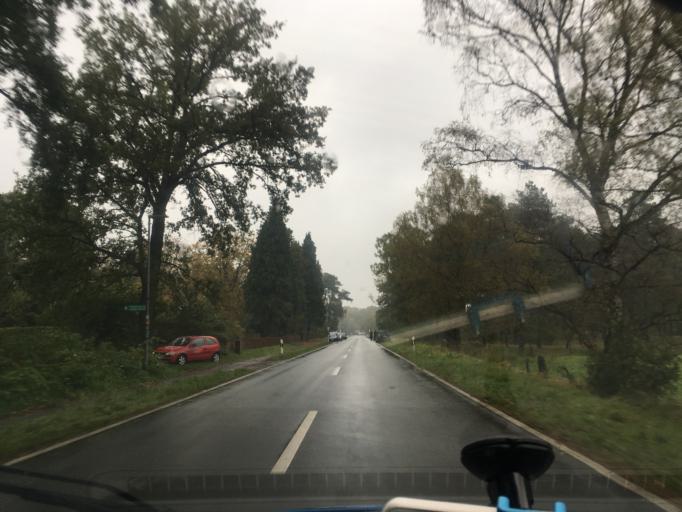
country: DE
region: Lower Saxony
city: Bispingen
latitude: 53.0767
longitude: 9.9946
